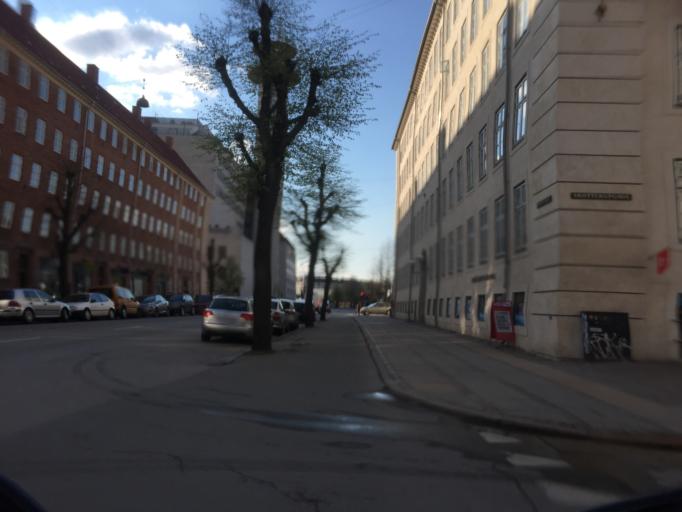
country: DK
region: Capital Region
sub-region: Frederiksberg Kommune
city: Frederiksberg
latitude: 55.6904
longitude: 12.5401
